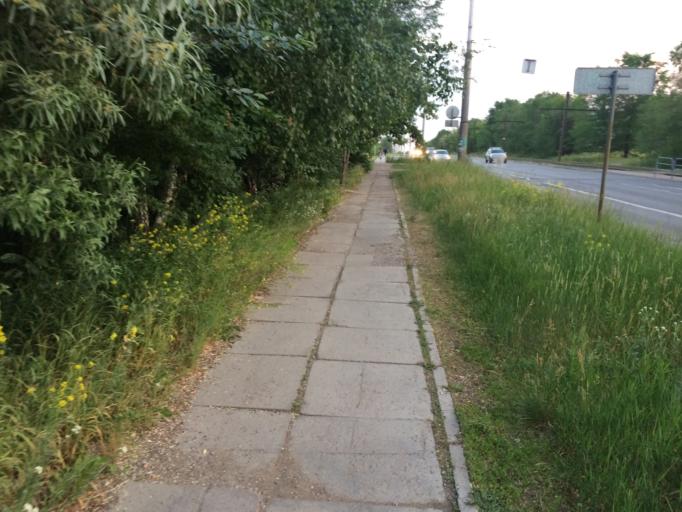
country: RU
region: Chelyabinsk
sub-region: Gorod Magnitogorsk
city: Magnitogorsk
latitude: 53.4175
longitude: 58.9619
